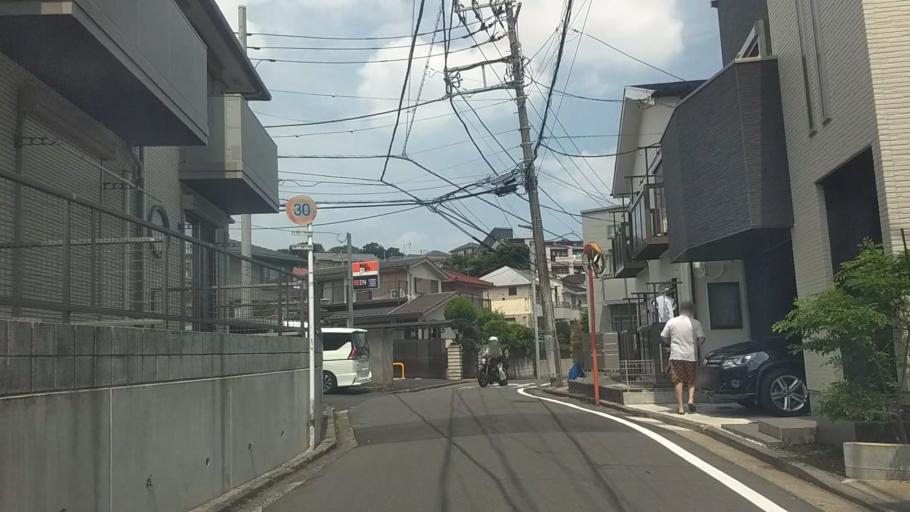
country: JP
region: Kanagawa
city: Yokohama
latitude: 35.5090
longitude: 139.6248
